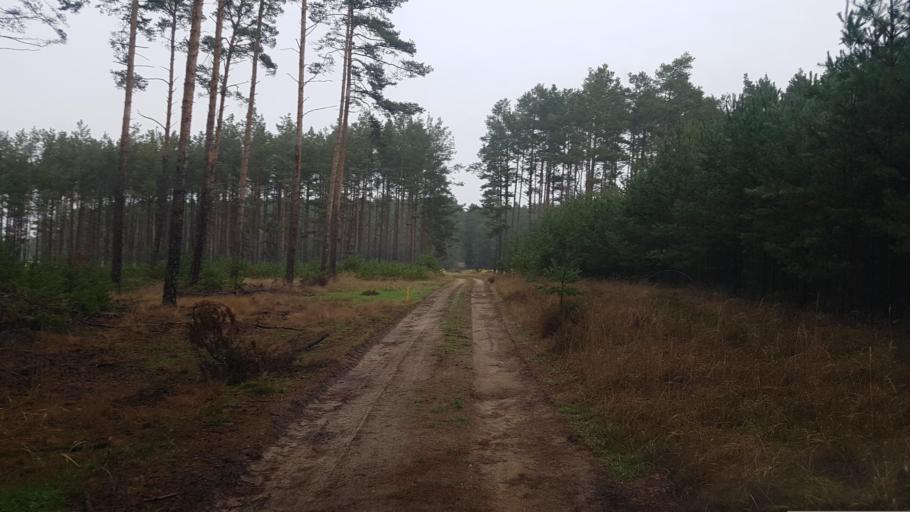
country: DE
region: Brandenburg
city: Sallgast
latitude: 51.6501
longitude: 13.8178
